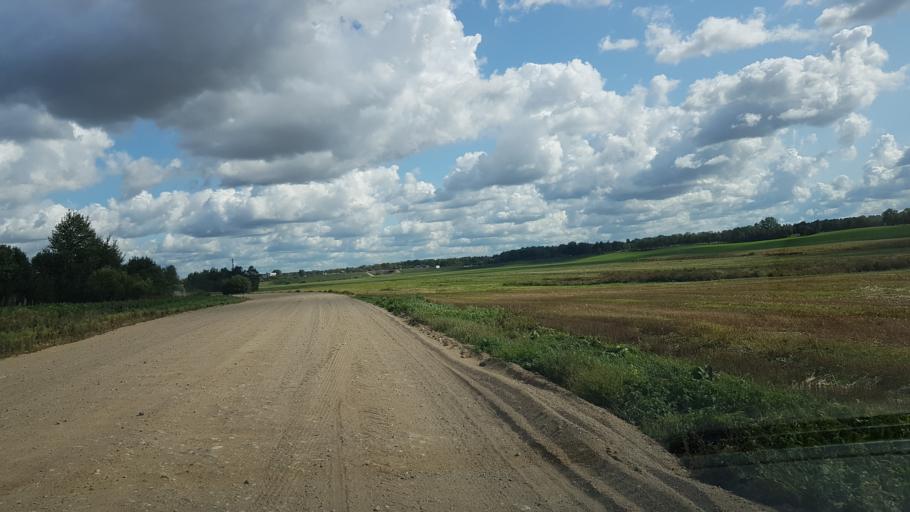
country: BY
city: Fanipol
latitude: 53.7371
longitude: 27.2832
